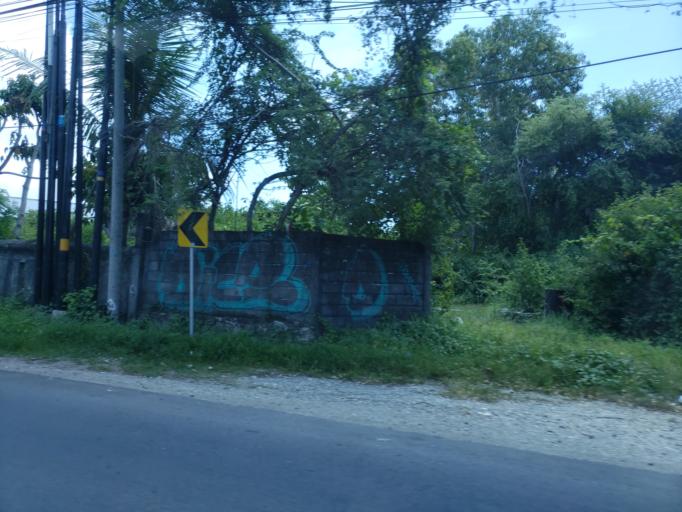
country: ID
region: Bali
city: Kangin
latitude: -8.8281
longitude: 115.1389
